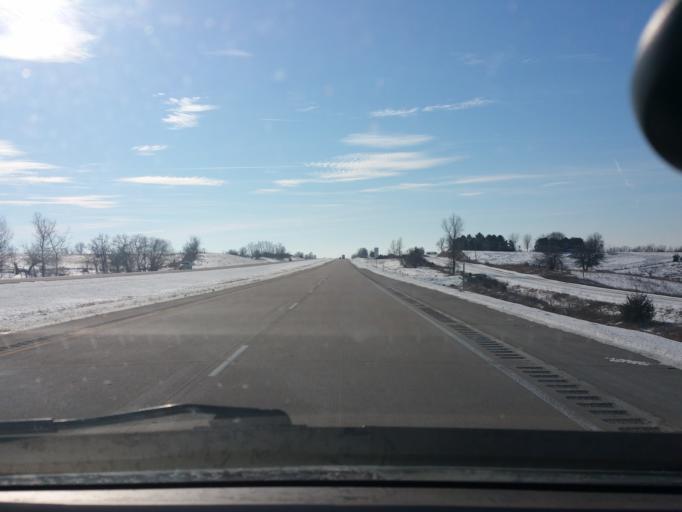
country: US
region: Iowa
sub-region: Decatur County
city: Leon
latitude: 40.8616
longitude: -93.8033
